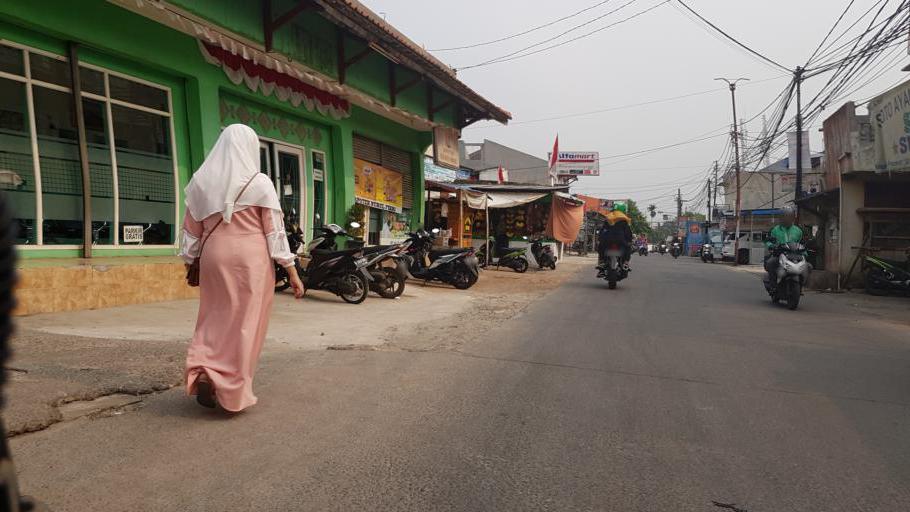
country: ID
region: West Java
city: Depok
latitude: -6.3619
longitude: 106.8430
